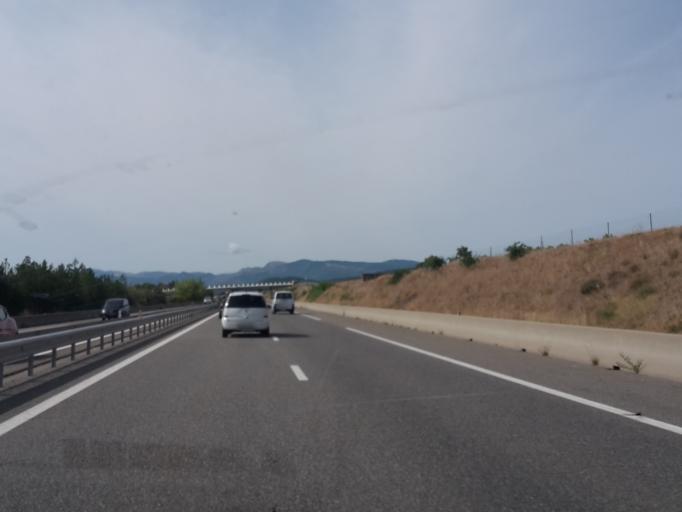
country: FR
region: Provence-Alpes-Cote d'Azur
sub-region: Departement des Hautes-Alpes
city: Tallard
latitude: 44.3903
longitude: 5.9399
